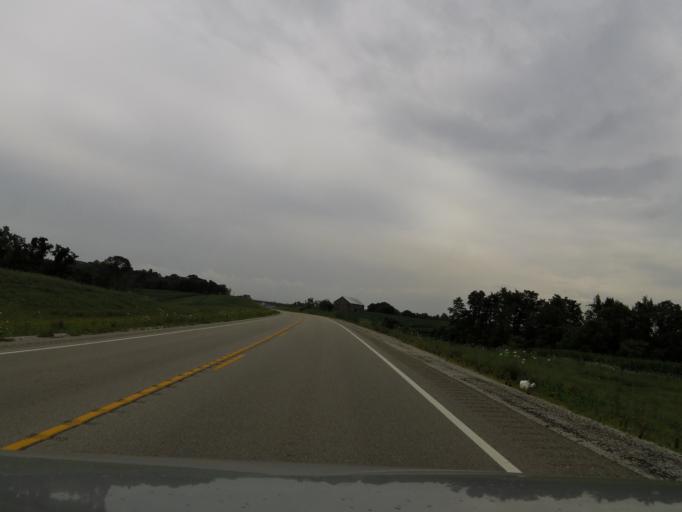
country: US
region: Ohio
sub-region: Brown County
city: Aberdeen
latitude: 38.6152
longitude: -83.8374
